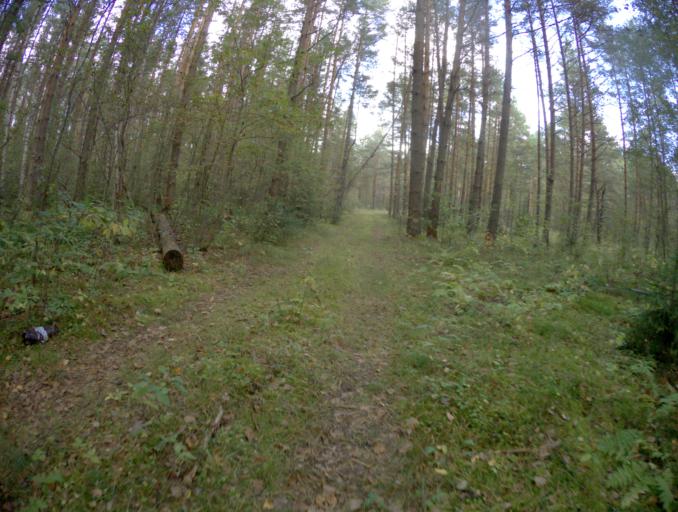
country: RU
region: Vladimir
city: Golovino
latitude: 55.9100
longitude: 40.4337
